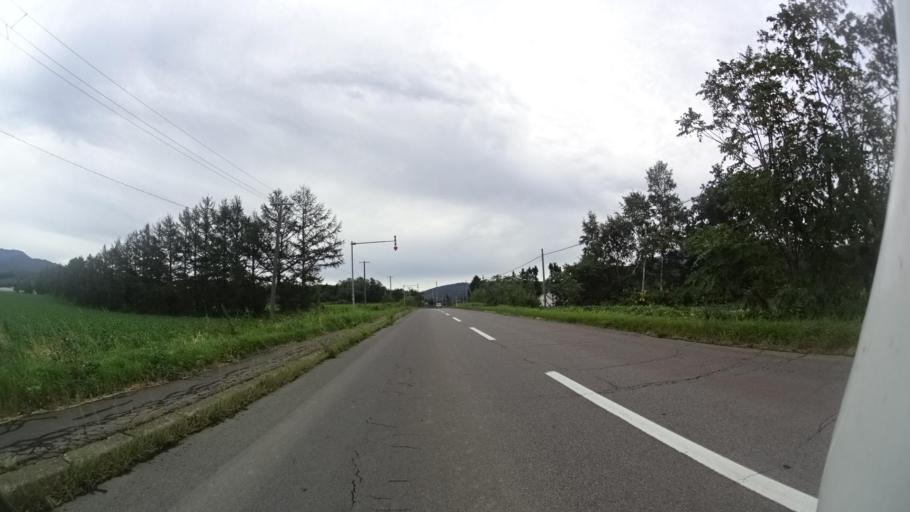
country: JP
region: Hokkaido
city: Shibetsu
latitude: 43.8732
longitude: 144.7475
